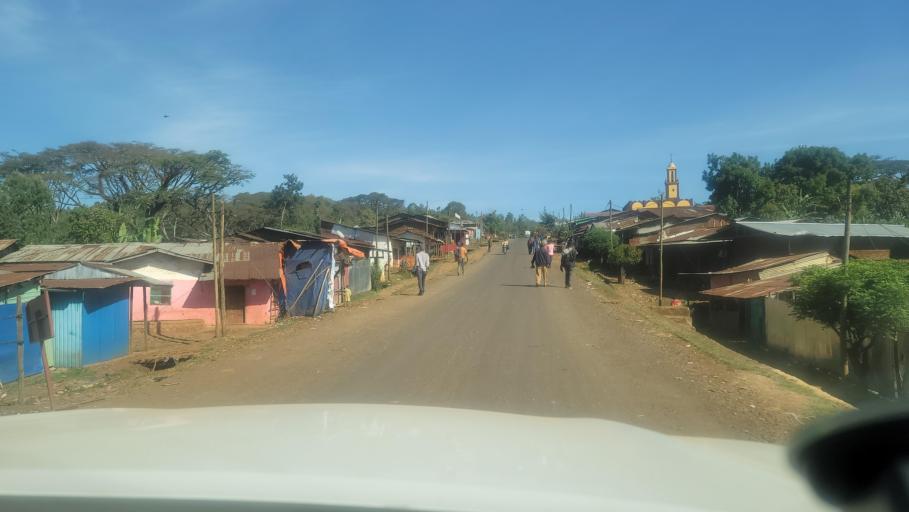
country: ET
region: Oromiya
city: Agaro
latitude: 7.7959
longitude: 36.4774
